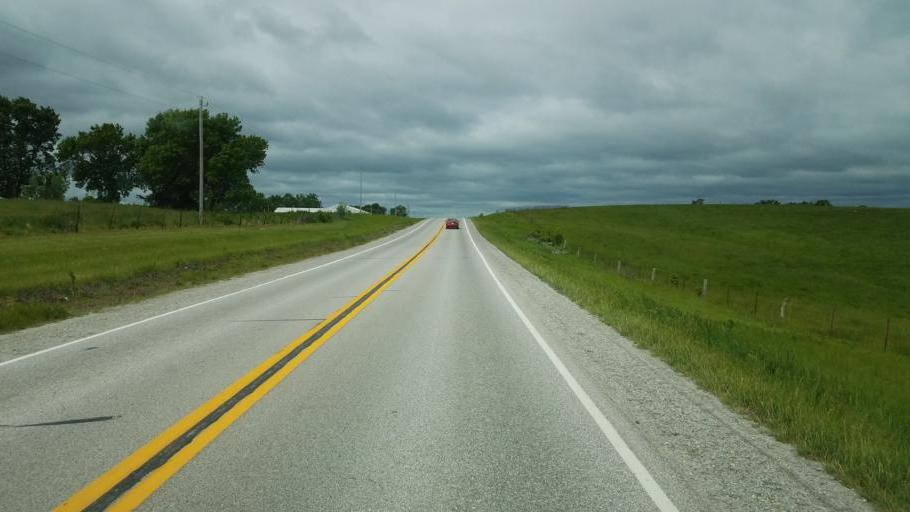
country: US
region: Iowa
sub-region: Decatur County
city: Lamoni
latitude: 40.6238
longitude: -93.8672
